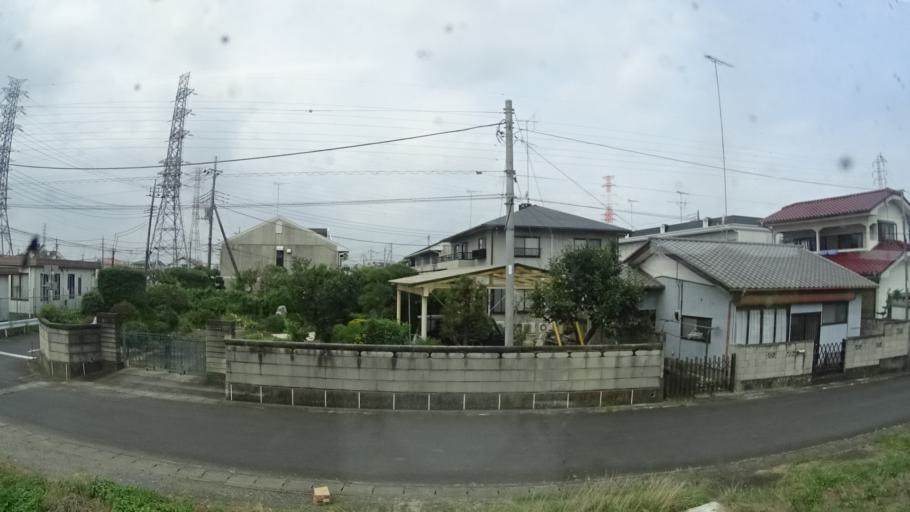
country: JP
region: Ibaraki
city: Shimodate
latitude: 36.3099
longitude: 139.9716
